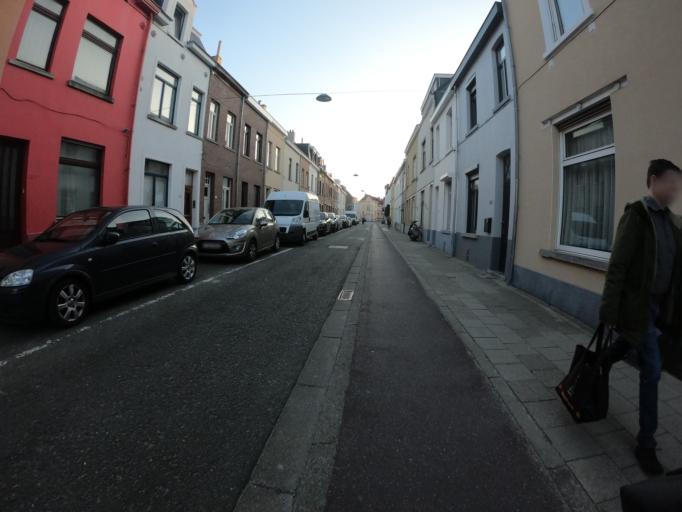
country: BE
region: Flanders
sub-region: Provincie Vlaams-Brabant
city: Kraainem
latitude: 50.8451
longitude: 4.4231
